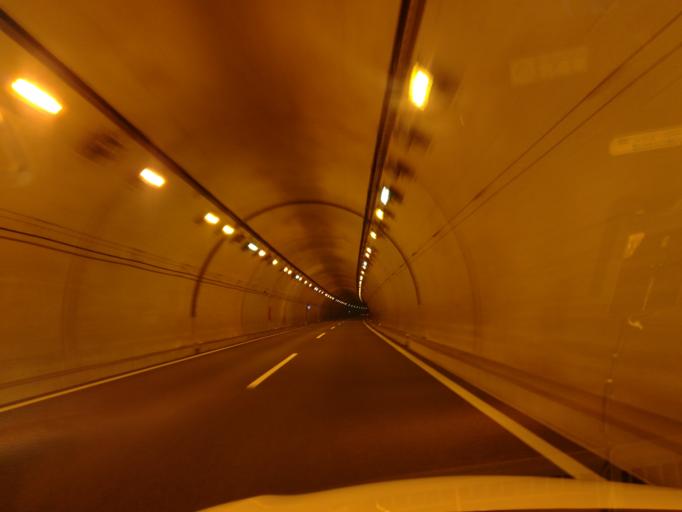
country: JP
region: Ehime
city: Kawanoecho
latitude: 33.8369
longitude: 133.6544
